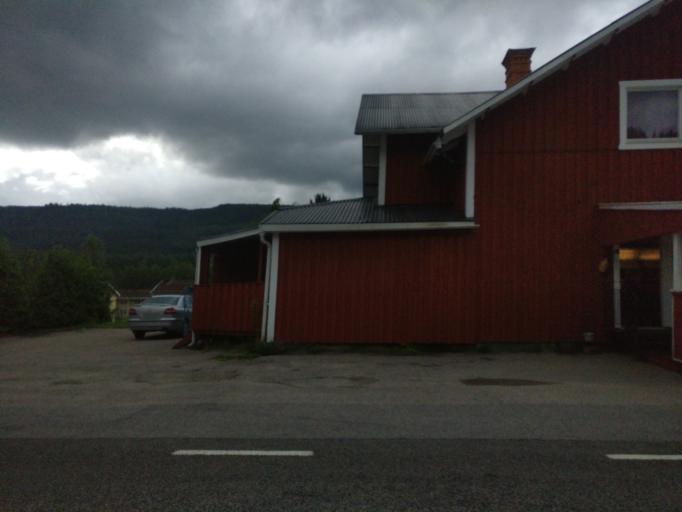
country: SE
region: Vaermland
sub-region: Torsby Kommun
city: Torsby
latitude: 60.7302
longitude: 12.8711
